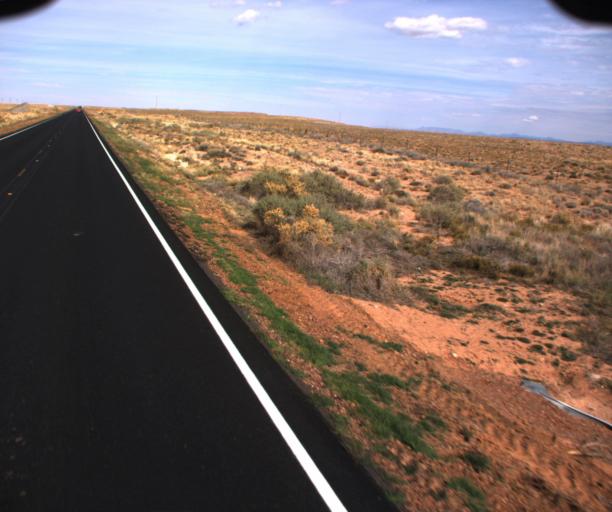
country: US
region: Arizona
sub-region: Apache County
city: Chinle
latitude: 36.0315
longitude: -109.6065
